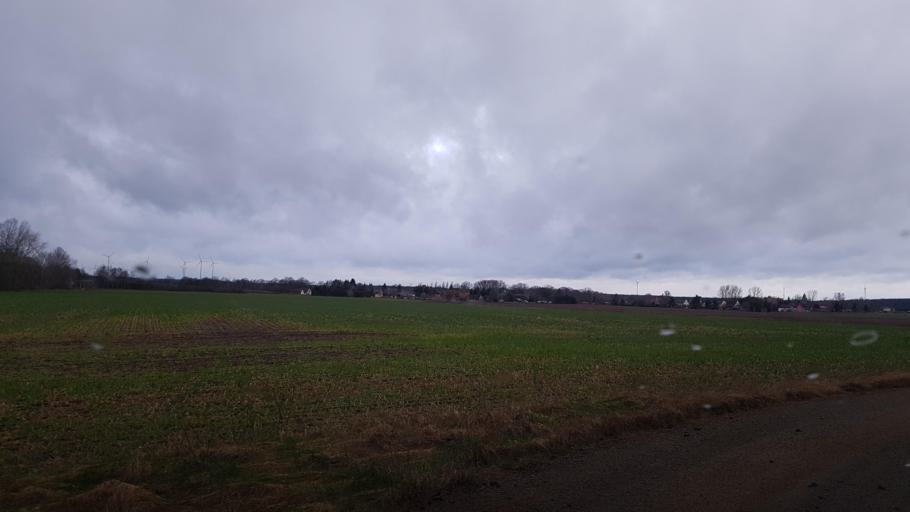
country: DE
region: Brandenburg
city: Bronkow
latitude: 51.6419
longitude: 13.9380
